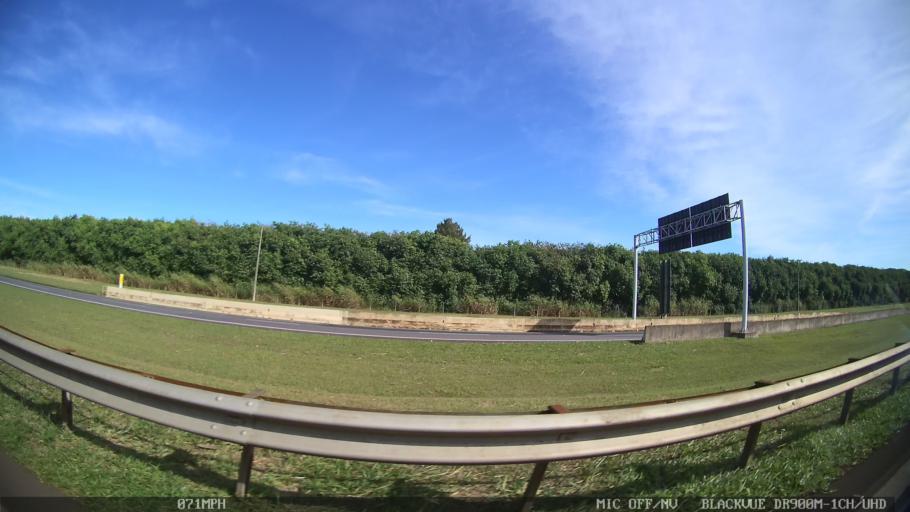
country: BR
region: Sao Paulo
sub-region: Cordeiropolis
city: Cordeiropolis
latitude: -22.4598
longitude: -47.3987
